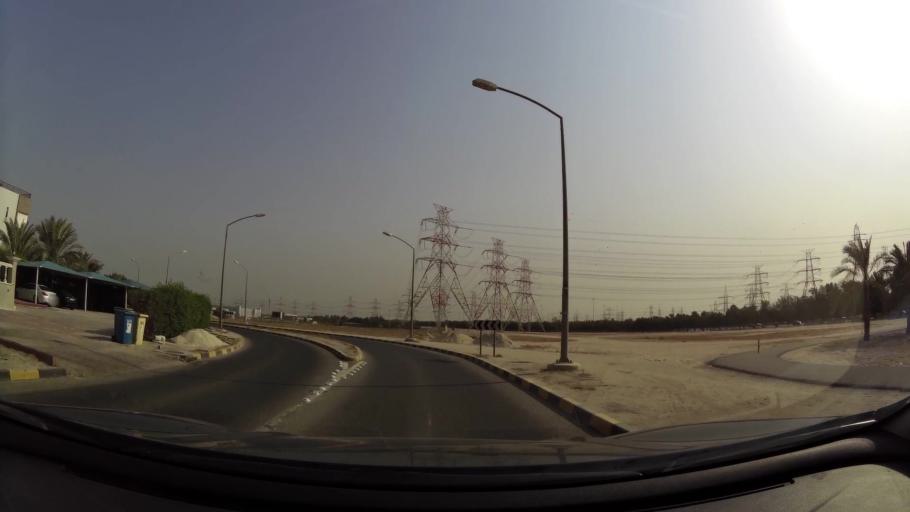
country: KW
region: Mubarak al Kabir
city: Sabah as Salim
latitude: 29.2730
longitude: 48.0403
